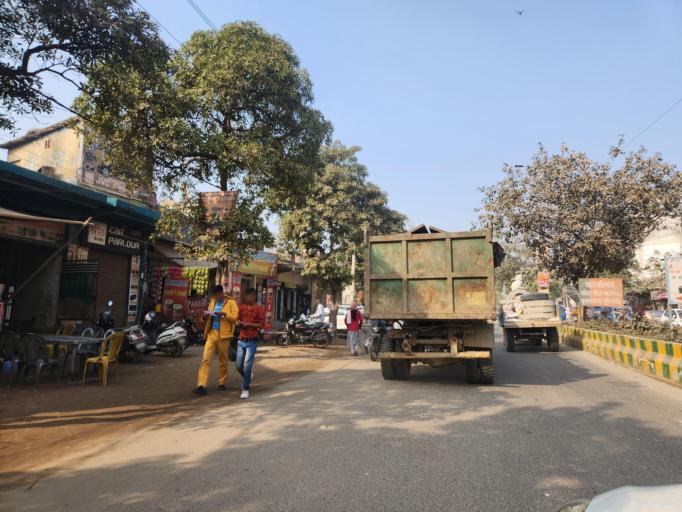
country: IN
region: Uttar Pradesh
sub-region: Ghaziabad
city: Ghaziabad
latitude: 28.6772
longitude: 77.4165
